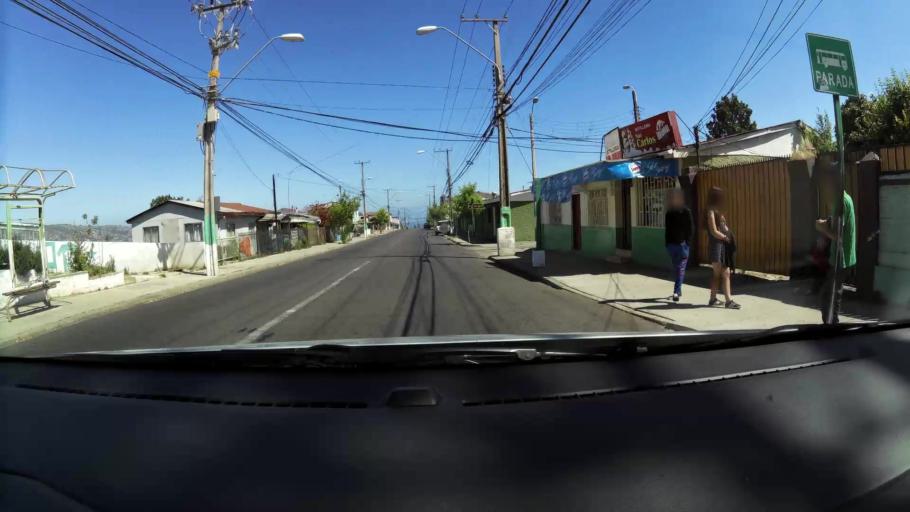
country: CL
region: Valparaiso
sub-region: Provincia de Valparaiso
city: Vina del Mar
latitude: -33.0503
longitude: -71.5854
